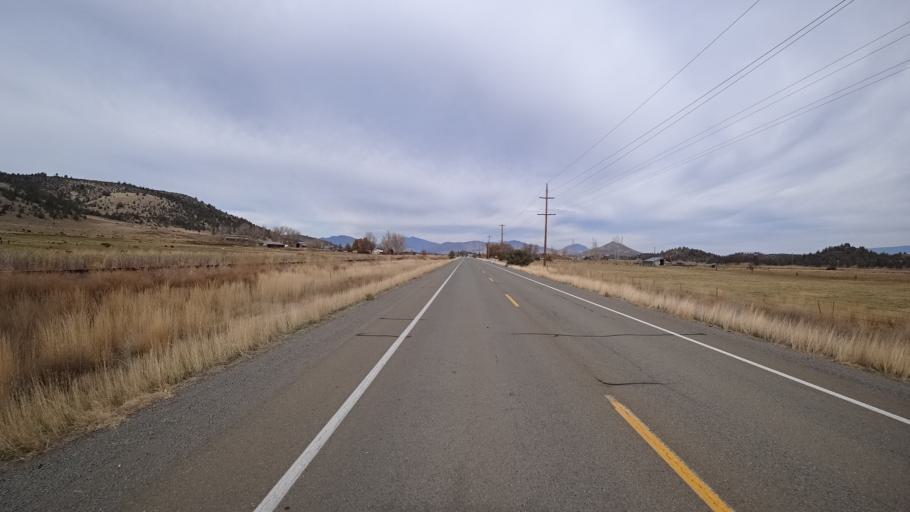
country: US
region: California
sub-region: Siskiyou County
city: Montague
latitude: 41.6702
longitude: -122.5239
